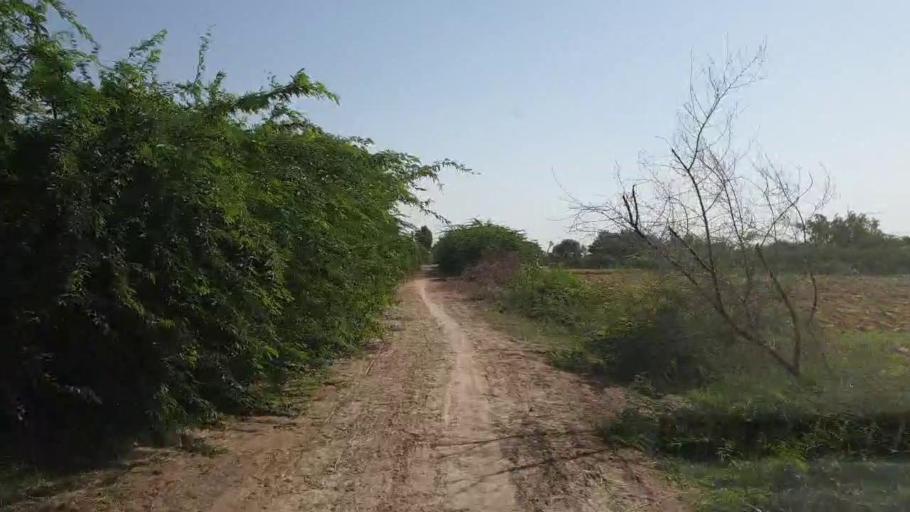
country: PK
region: Sindh
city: Kadhan
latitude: 24.5841
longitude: 69.0115
